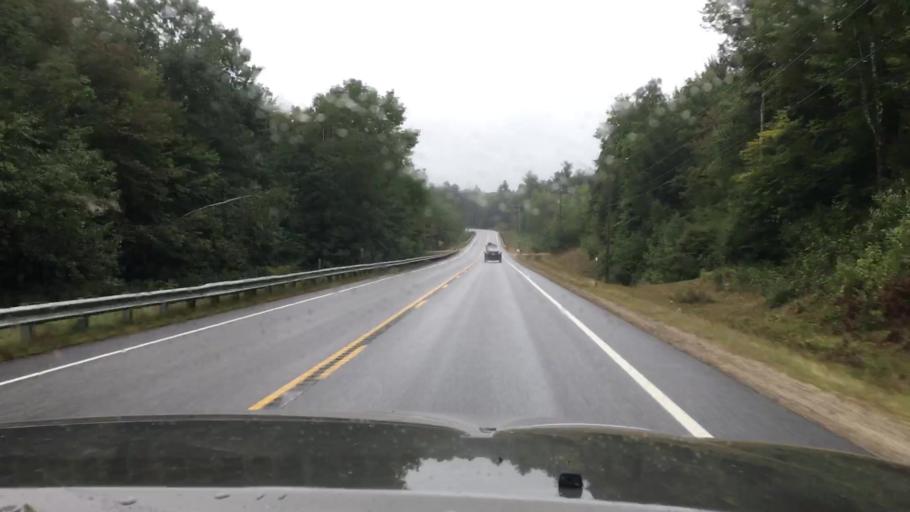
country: US
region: New Hampshire
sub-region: Cheshire County
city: Harrisville
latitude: 43.0523
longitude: -72.0779
